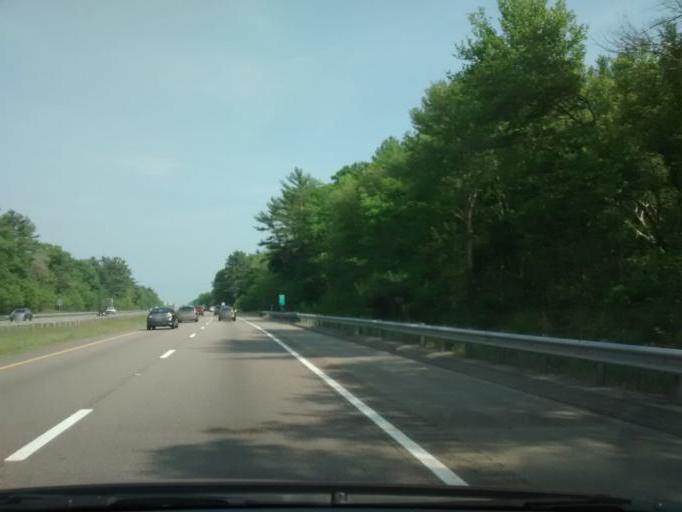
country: US
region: Massachusetts
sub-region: Plymouth County
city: Middleborough Center
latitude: 41.8962
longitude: -70.9548
